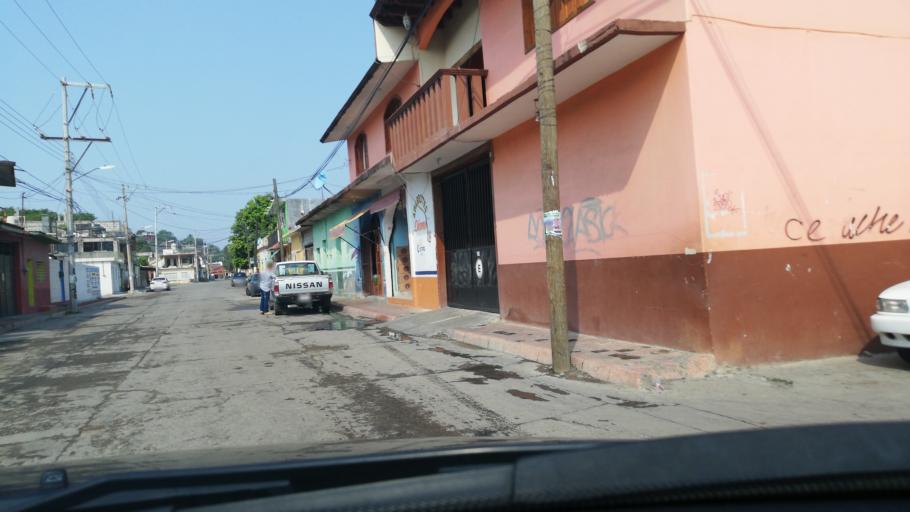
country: MX
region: Oaxaca
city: San Blas Atempa
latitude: 16.3375
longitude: -95.2257
